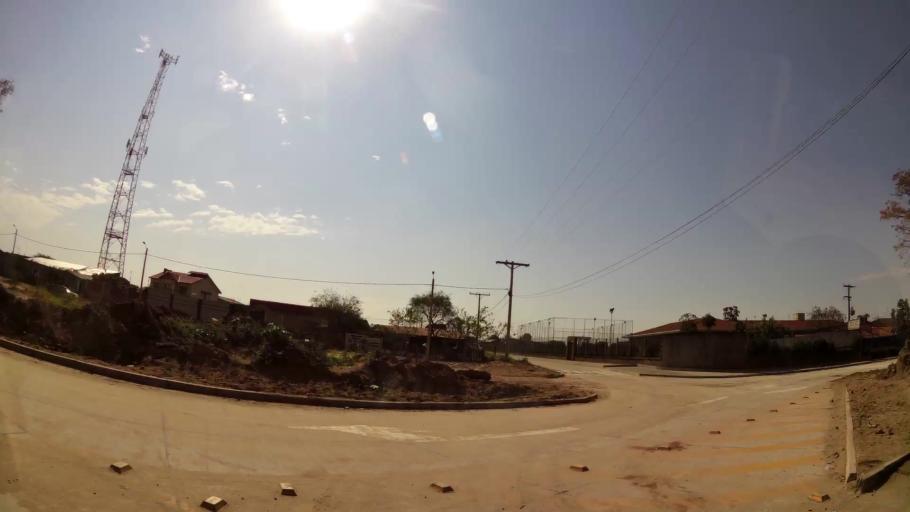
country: BO
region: Santa Cruz
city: Cotoca
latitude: -17.7533
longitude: -63.0975
